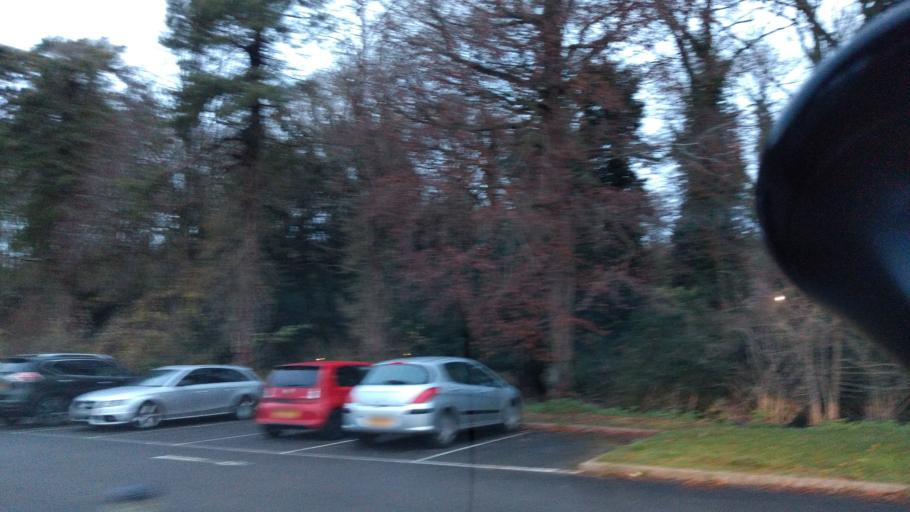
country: GB
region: England
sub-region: Oxfordshire
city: Shrivenham
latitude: 51.6059
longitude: -1.6390
